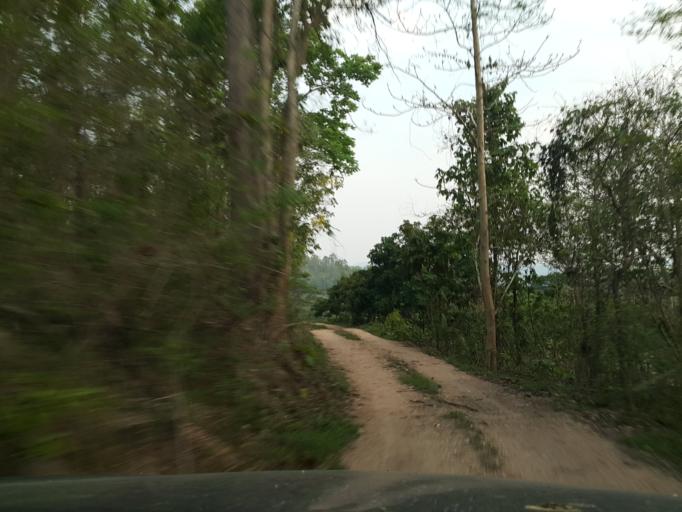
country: TH
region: Lamphun
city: Thung Hua Chang
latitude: 17.8950
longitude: 99.0851
